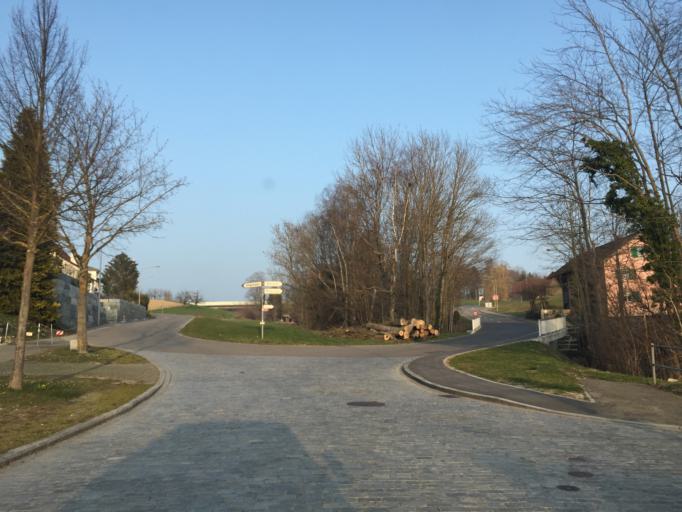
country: CH
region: Zurich
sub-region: Bezirk Andelfingen
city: Dachsen
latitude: 47.6635
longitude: 8.6206
